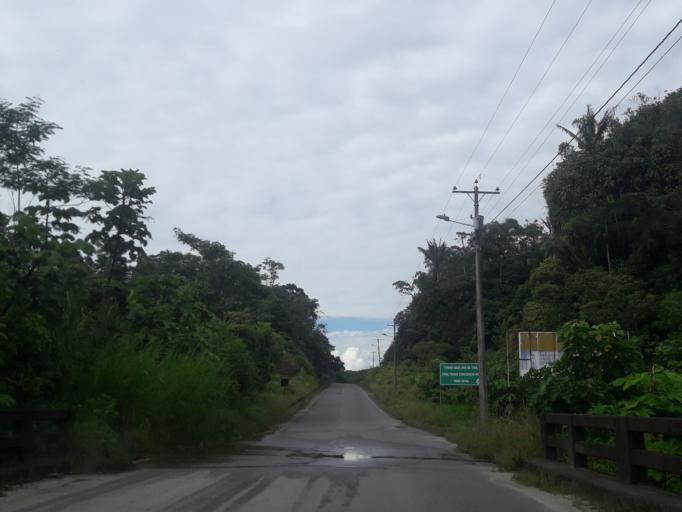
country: EC
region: Napo
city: Tena
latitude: -1.0412
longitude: -77.8983
